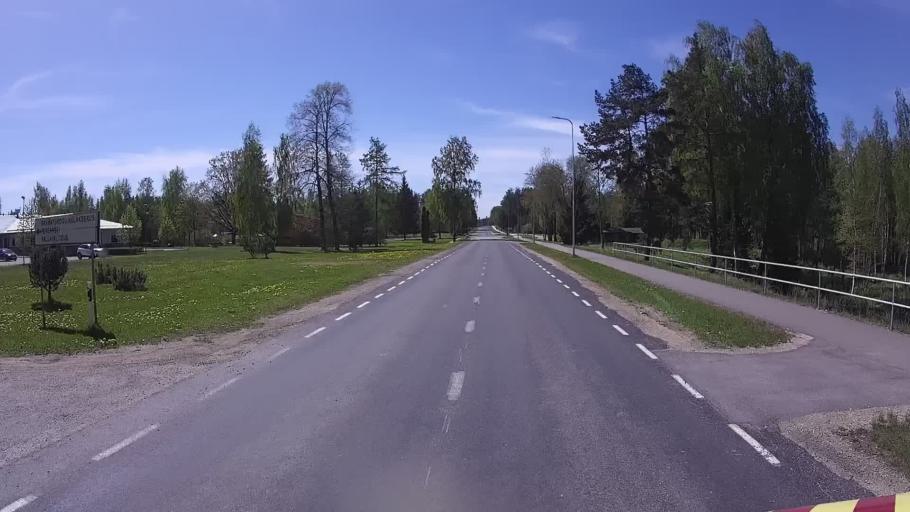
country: EE
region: Polvamaa
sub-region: Raepina vald
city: Rapina
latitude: 58.0055
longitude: 27.3473
